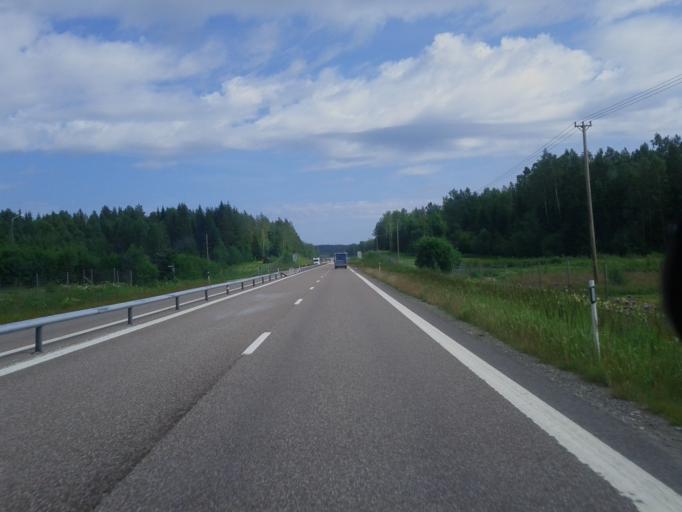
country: SE
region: Vaesternorrland
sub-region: OErnskoeldsviks Kommun
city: Husum
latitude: 63.3199
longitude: 19.0271
